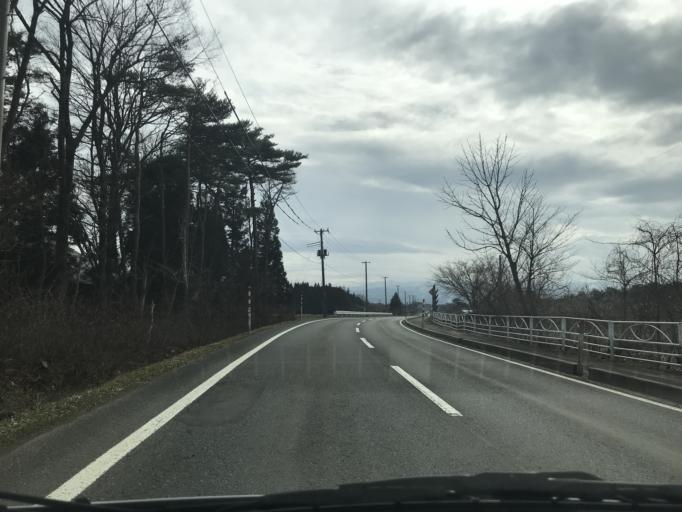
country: JP
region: Iwate
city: Hanamaki
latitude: 39.3721
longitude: 141.0034
